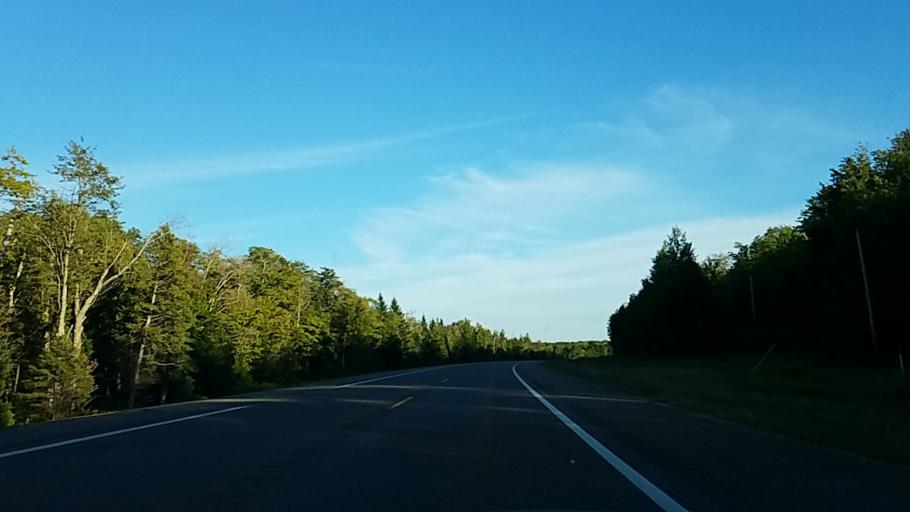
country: US
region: Michigan
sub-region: Alger County
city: Munising
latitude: 46.4587
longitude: -86.8929
